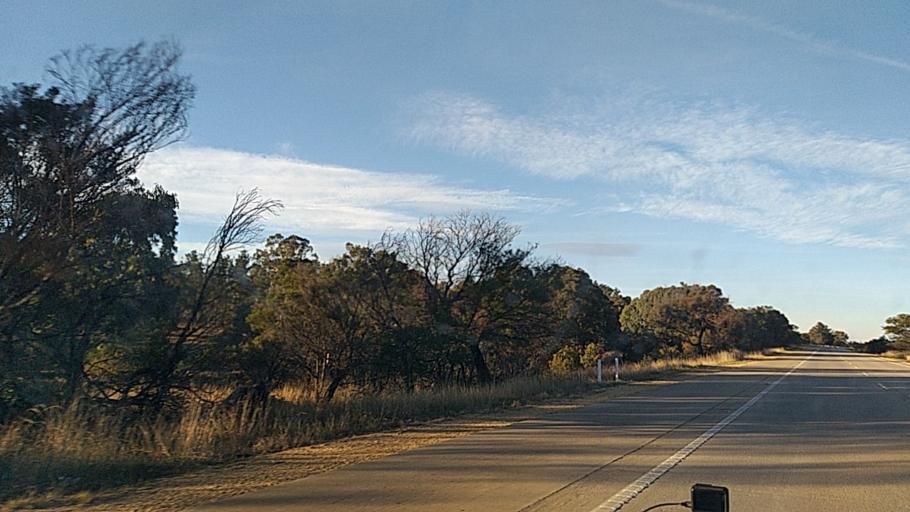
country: AU
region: New South Wales
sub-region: Yass Valley
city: Gundaroo
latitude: -35.1305
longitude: 149.3416
